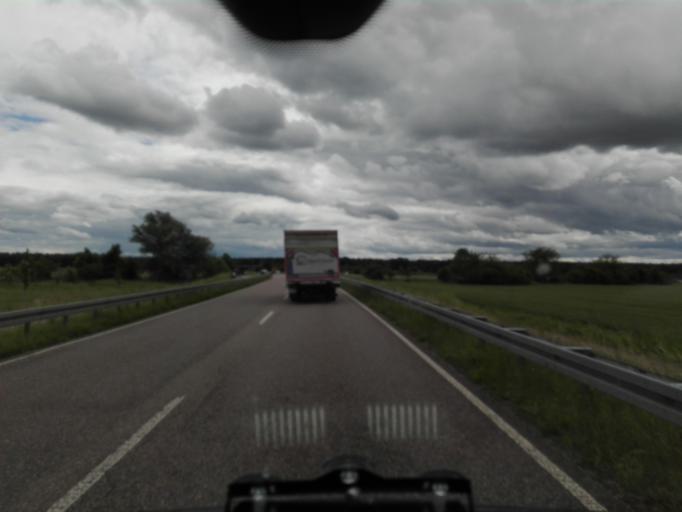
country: DE
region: Baden-Wuerttemberg
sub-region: Karlsruhe Region
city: Graben-Neudorf
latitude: 49.1400
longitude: 8.4706
